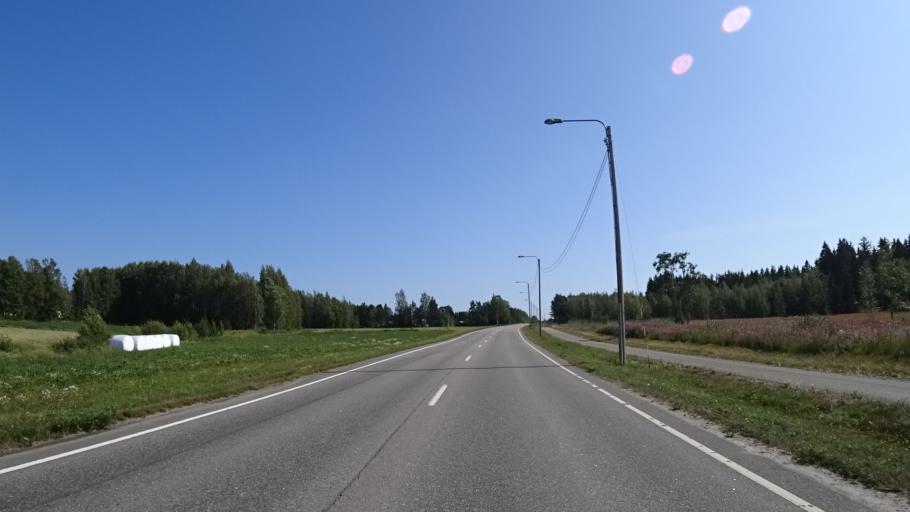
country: FI
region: Kymenlaakso
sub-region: Kotka-Hamina
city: Karhula
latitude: 60.5368
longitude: 26.9337
